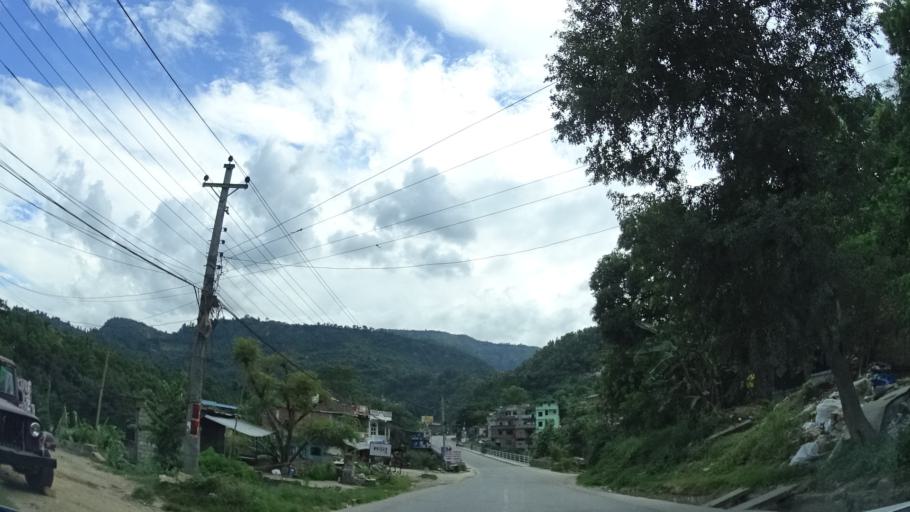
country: NP
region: Central Region
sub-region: Narayani Zone
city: Bharatpur
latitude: 27.8083
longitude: 84.8347
